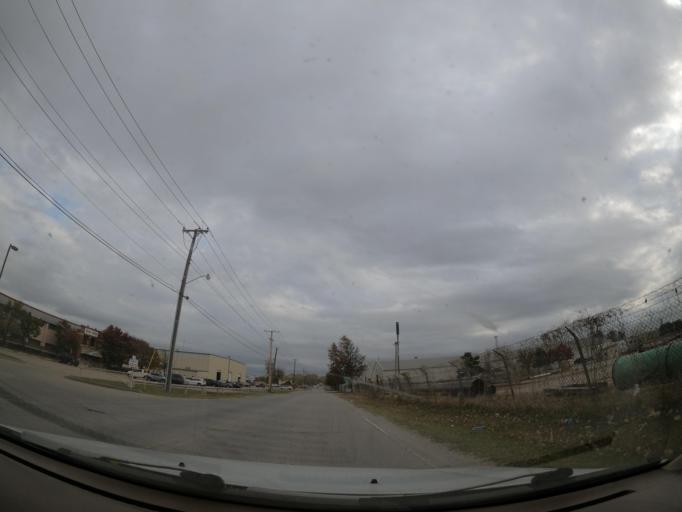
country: US
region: Oklahoma
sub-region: Tulsa County
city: Tulsa
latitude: 36.1043
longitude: -95.9964
